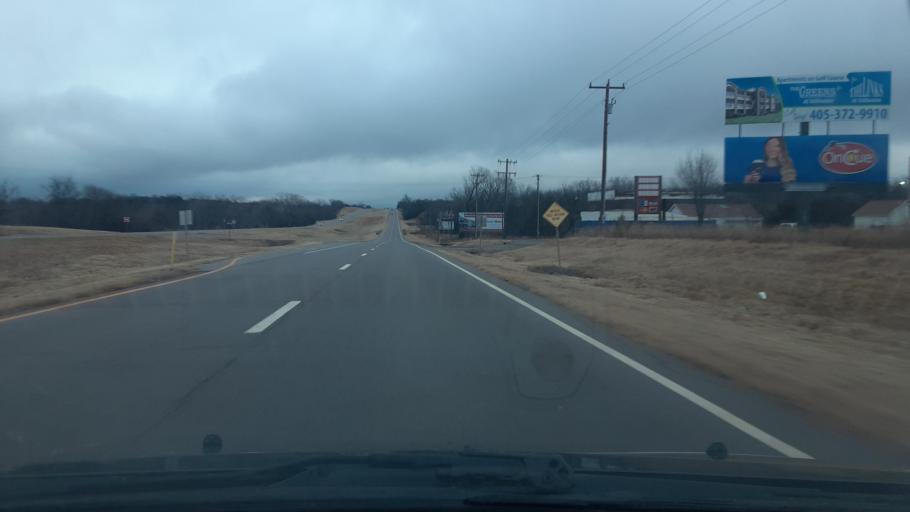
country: US
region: Oklahoma
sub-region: Payne County
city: Stillwater
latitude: 36.1158
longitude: -97.1597
